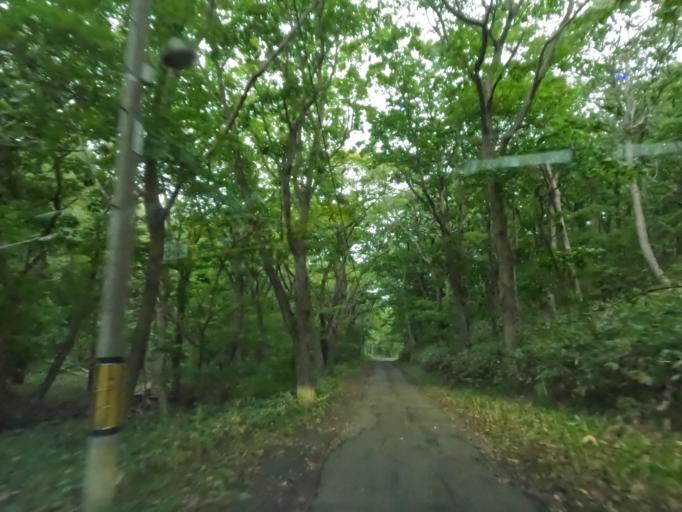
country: JP
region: Hokkaido
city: Muroran
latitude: 42.3698
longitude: 140.9743
